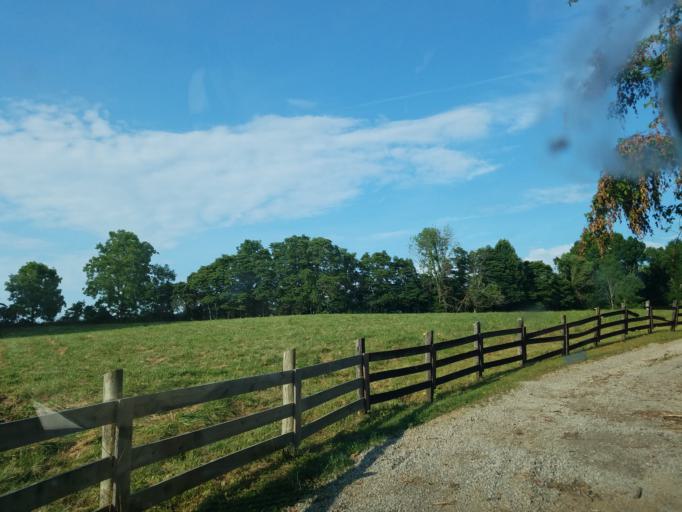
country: US
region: Ohio
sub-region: Adams County
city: West Union
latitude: 38.8696
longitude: -83.4813
